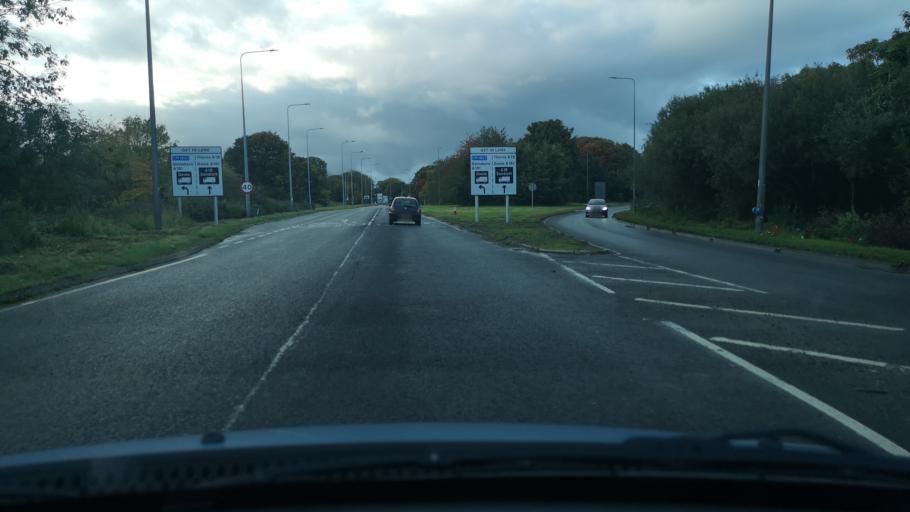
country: GB
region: England
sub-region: North Lincolnshire
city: Crowle
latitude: 53.5847
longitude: -0.8157
